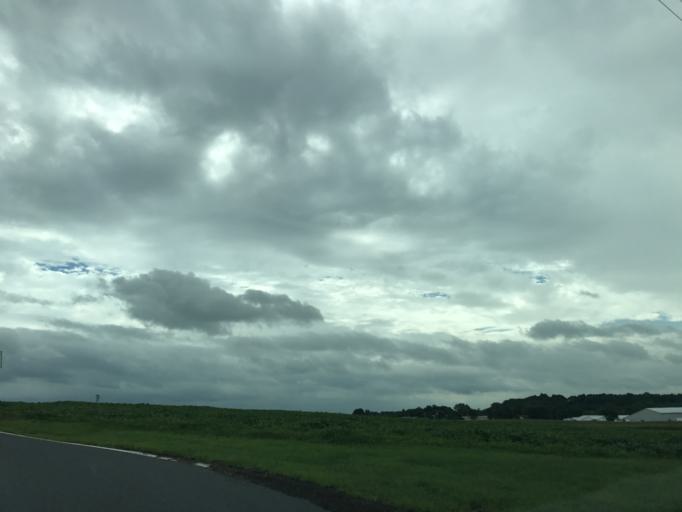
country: US
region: Pennsylvania
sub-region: Lancaster County
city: East Petersburg
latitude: 40.0862
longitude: -76.3710
